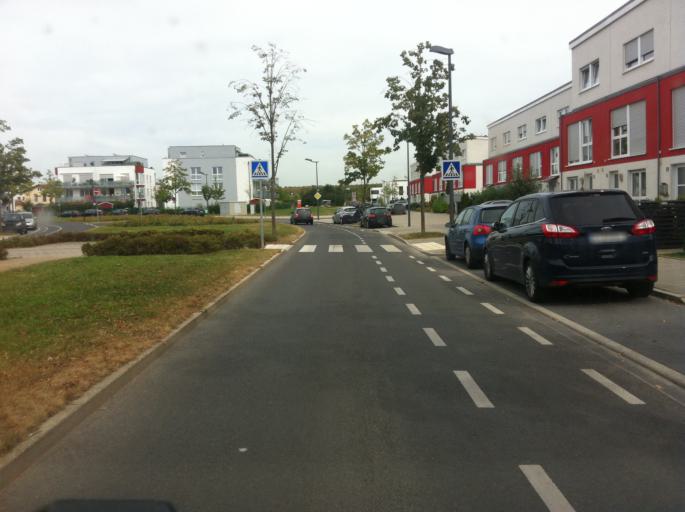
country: DE
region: North Rhine-Westphalia
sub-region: Regierungsbezirk Koln
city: Mengenich
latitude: 50.9635
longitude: 6.8421
